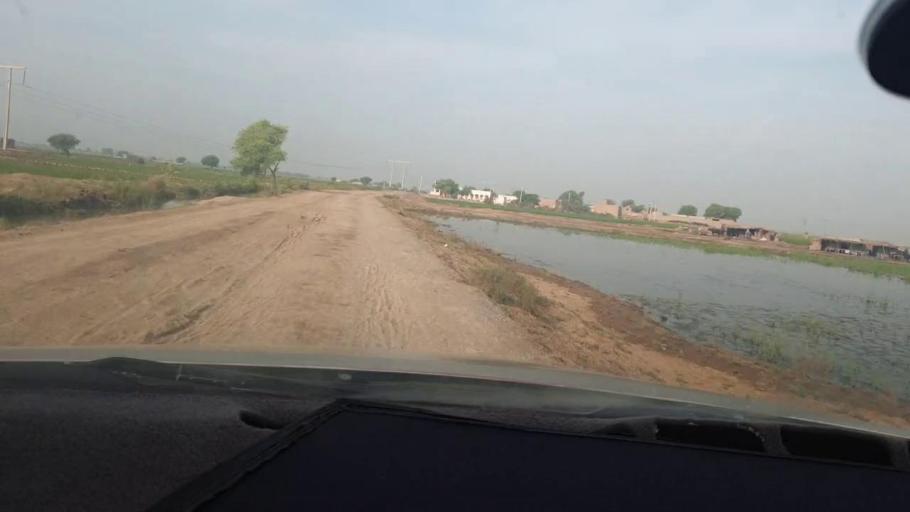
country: PK
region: Sindh
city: Jacobabad
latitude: 28.3358
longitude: 68.4049
